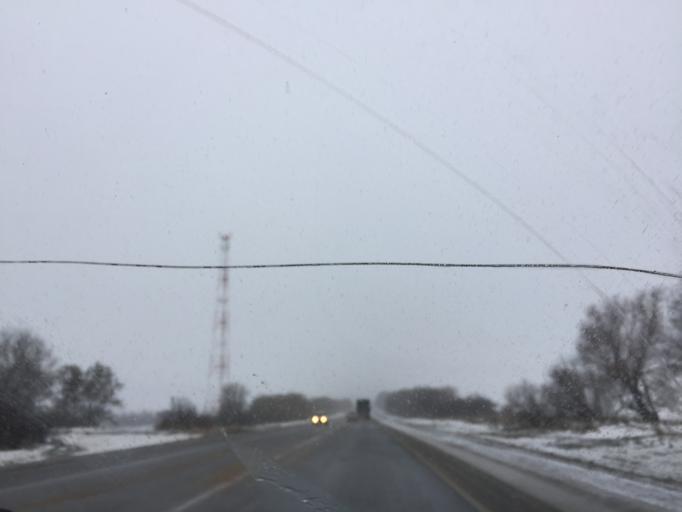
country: RU
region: Tula
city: Plavsk
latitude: 53.7858
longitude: 37.3643
